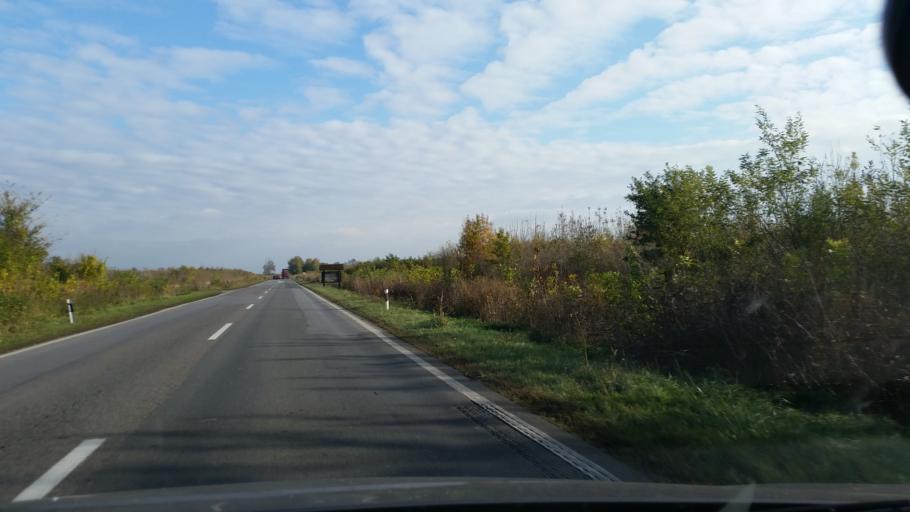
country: RS
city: Ecka
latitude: 45.3273
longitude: 20.4451
